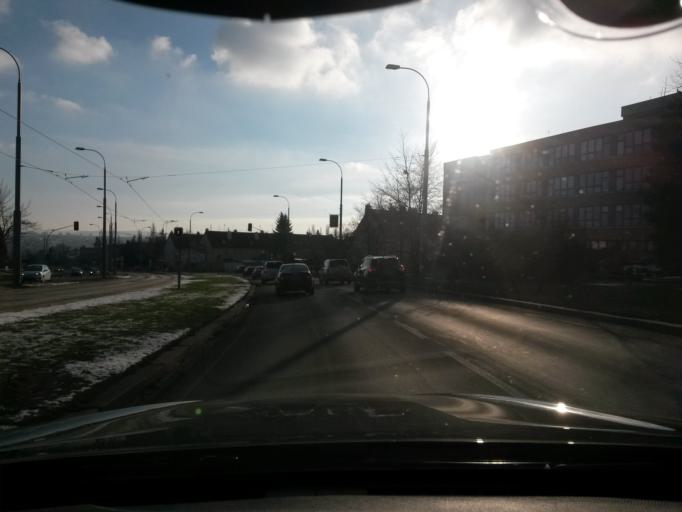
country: CZ
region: Plzensky
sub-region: Okres Plzen-Mesto
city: Pilsen
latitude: 49.7689
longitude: 13.3628
